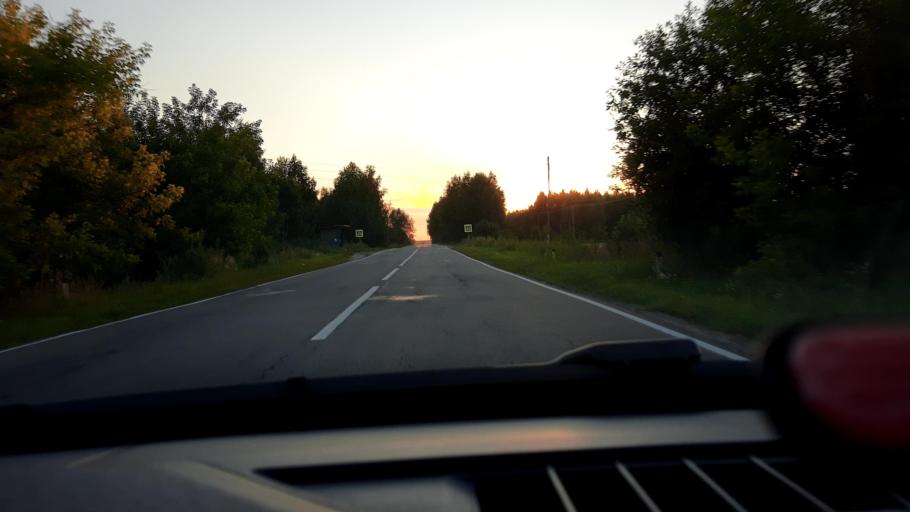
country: RU
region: Nizjnij Novgorod
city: Neklyudovo
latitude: 56.5230
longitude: 43.8726
